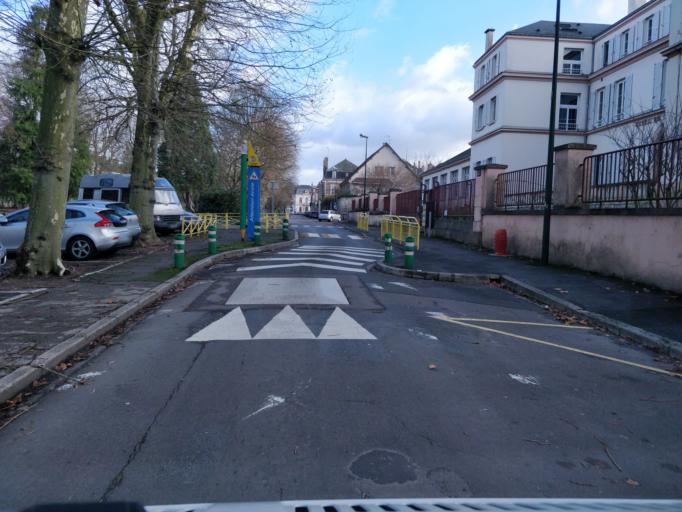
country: FR
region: Bourgogne
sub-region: Departement de l'Yonne
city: Sens
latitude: 48.1949
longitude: 3.2799
